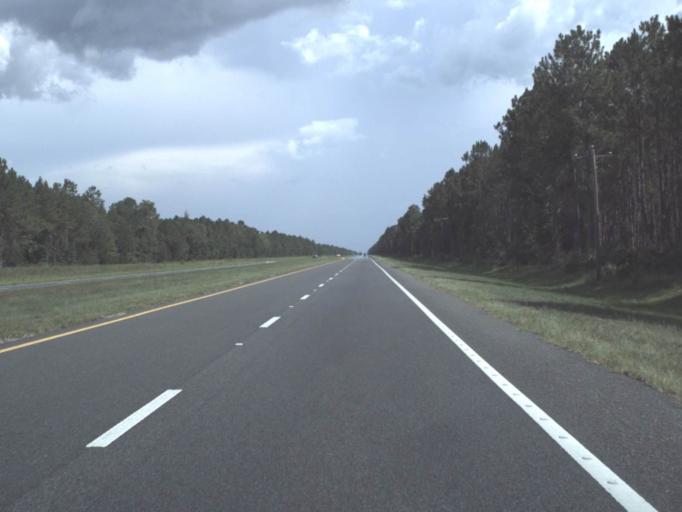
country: US
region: Florida
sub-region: Levy County
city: Chiefland
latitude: 29.3794
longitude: -82.8005
